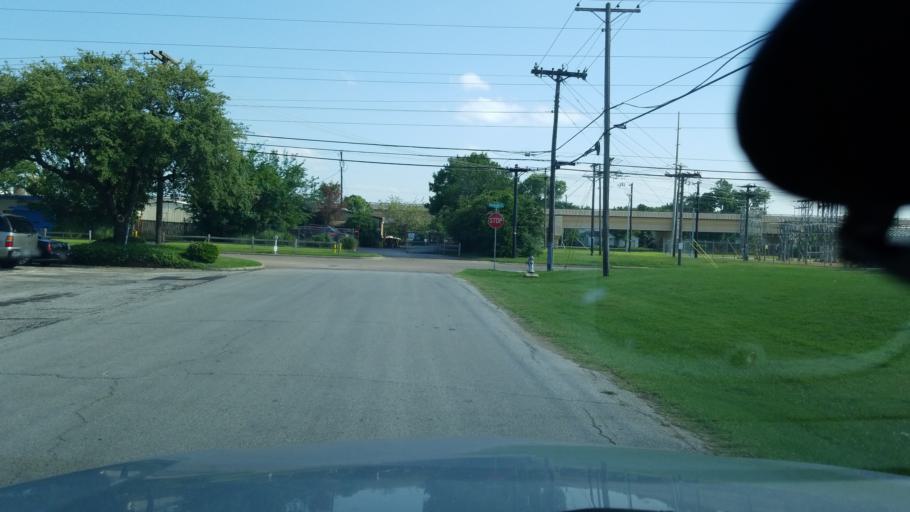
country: US
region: Texas
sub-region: Dallas County
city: Irving
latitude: 32.8166
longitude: -96.9738
